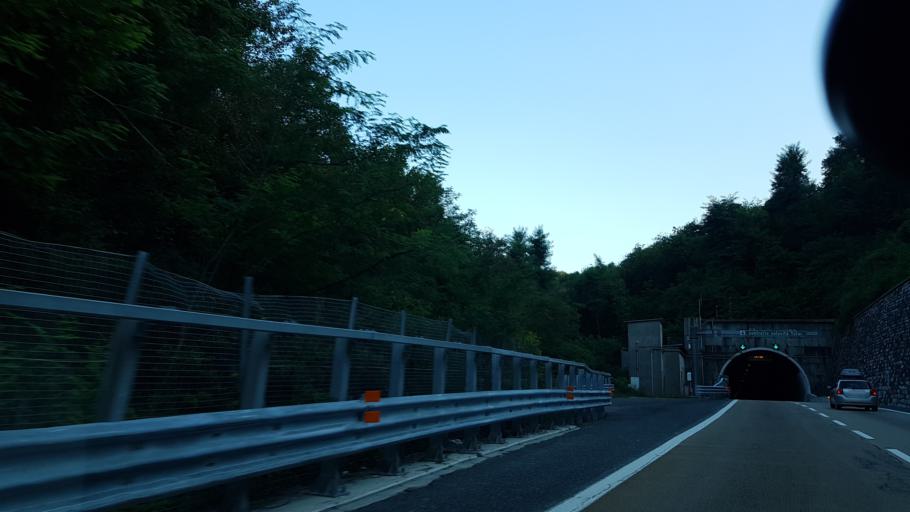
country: IT
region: Liguria
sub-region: Provincia di Genova
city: Busalla
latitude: 44.5604
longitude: 8.9470
